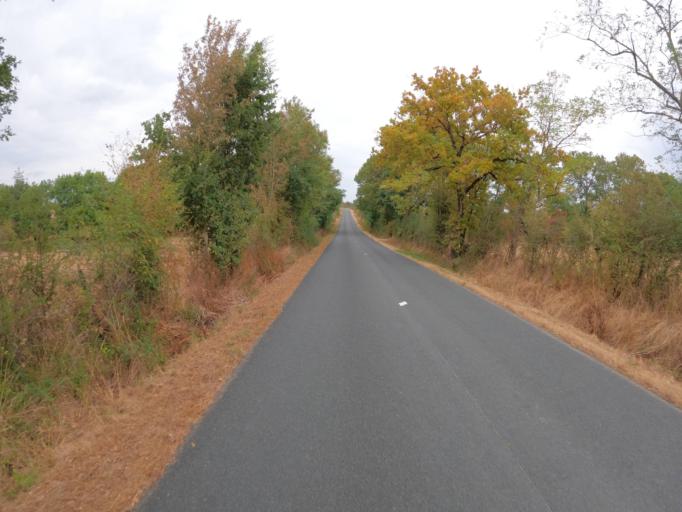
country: FR
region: Pays de la Loire
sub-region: Departement de la Vendee
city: Tiffauges
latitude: 46.9988
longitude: -1.1082
